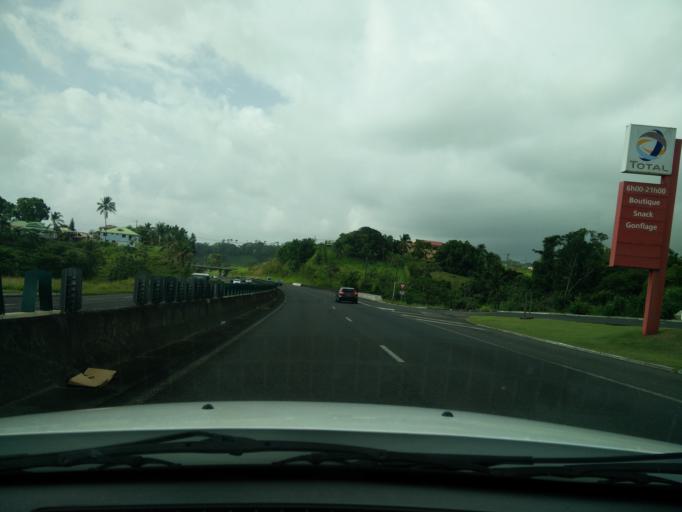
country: GP
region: Guadeloupe
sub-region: Guadeloupe
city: Petit-Bourg
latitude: 16.1875
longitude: -61.6074
